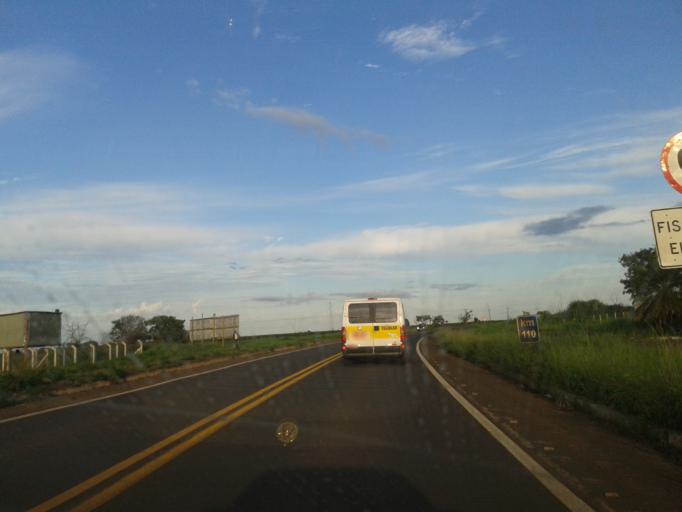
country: BR
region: Minas Gerais
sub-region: Araguari
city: Araguari
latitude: -18.6404
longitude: -48.2227
